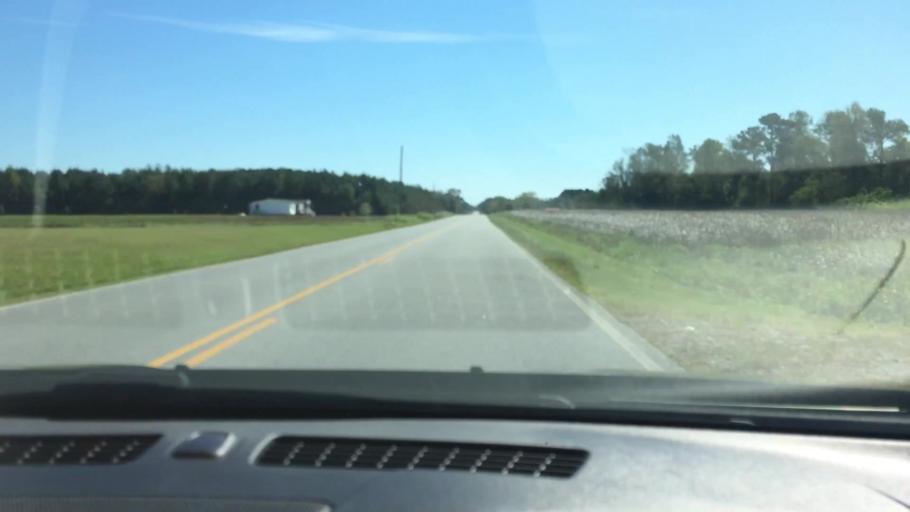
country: US
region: North Carolina
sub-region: Pitt County
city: Grifton
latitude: 35.3952
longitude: -77.3955
